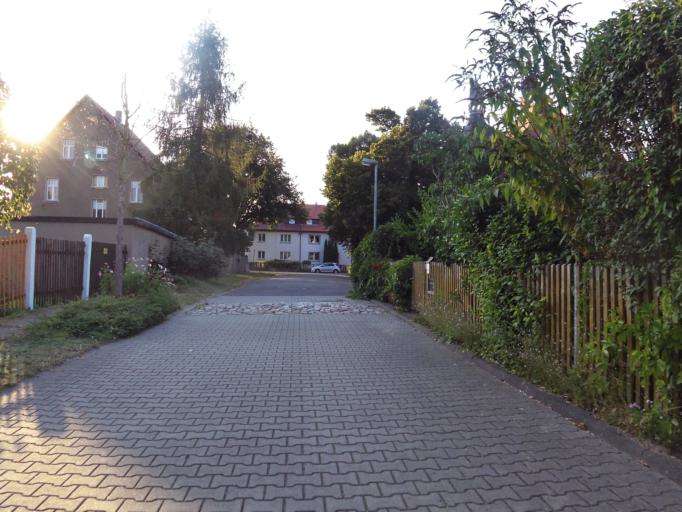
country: DE
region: Saxony
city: Leipzig
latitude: 51.3427
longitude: 12.3156
